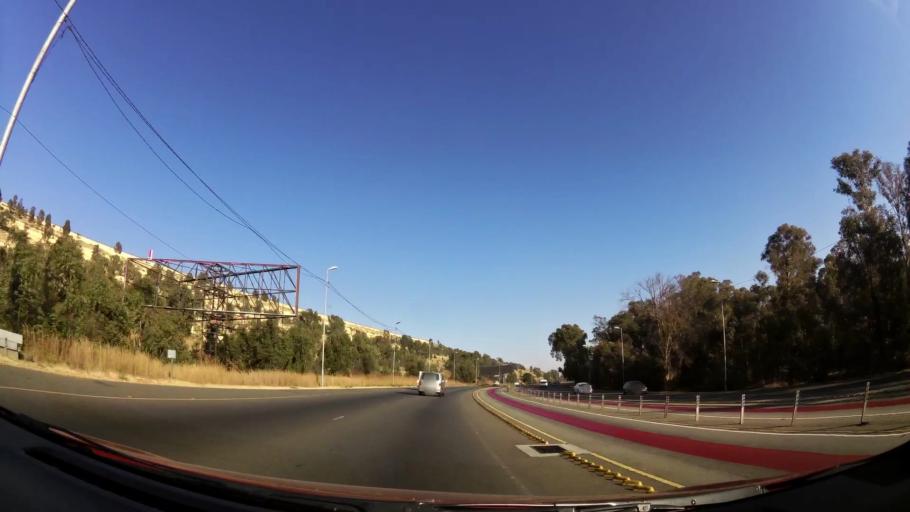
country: ZA
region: Gauteng
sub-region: City of Johannesburg Metropolitan Municipality
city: Johannesburg
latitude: -26.2342
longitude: 27.9725
